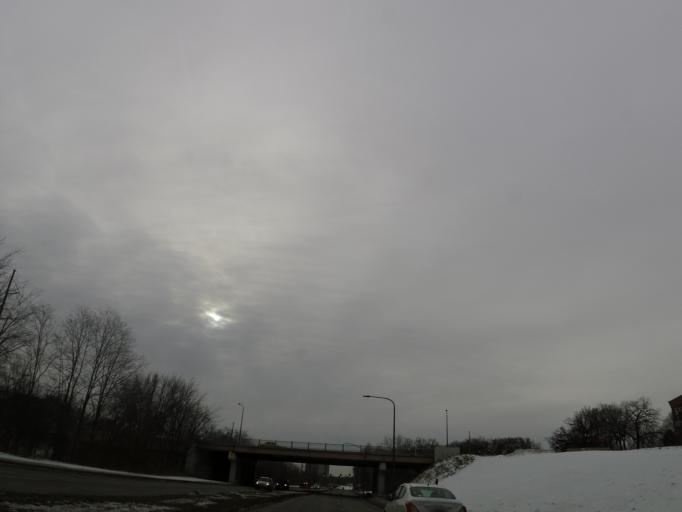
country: US
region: Minnesota
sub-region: Ramsey County
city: Falcon Heights
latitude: 44.9407
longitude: -93.1526
